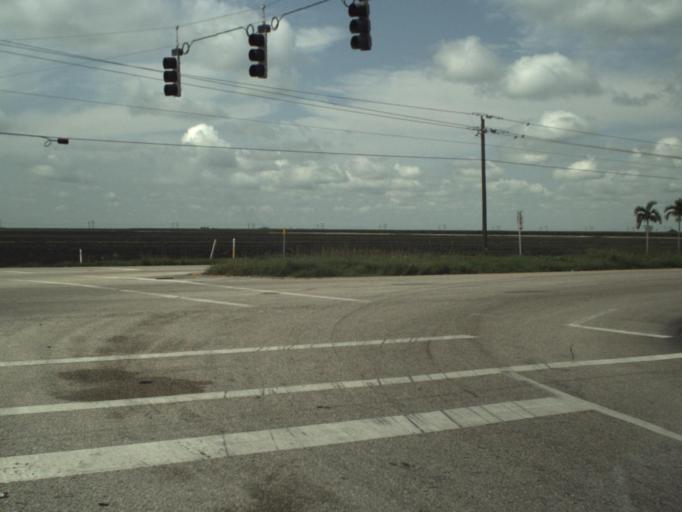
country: US
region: Florida
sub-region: Palm Beach County
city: Belle Glade Camp
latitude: 26.6640
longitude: -80.6870
